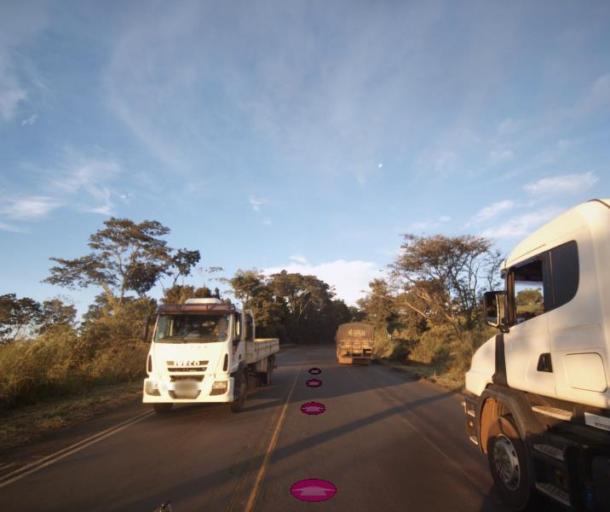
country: BR
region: Goias
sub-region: Abadiania
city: Abadiania
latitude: -16.1030
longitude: -48.8653
